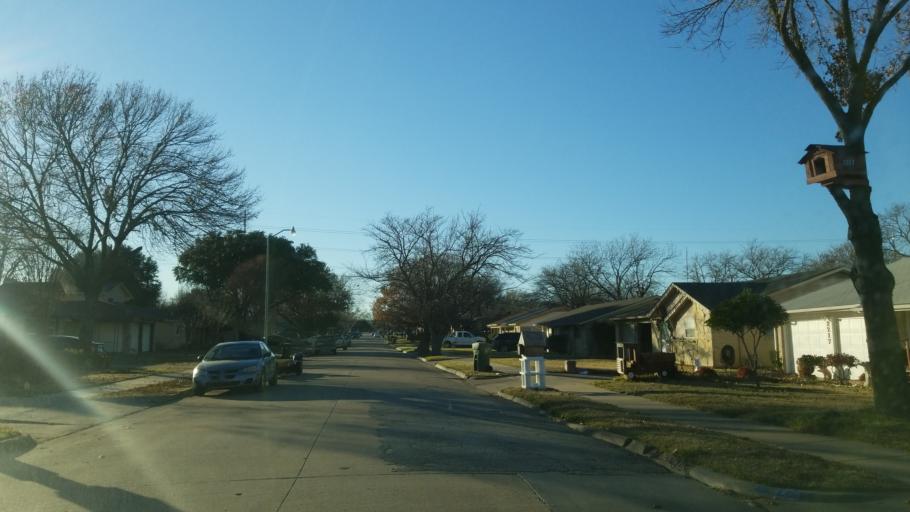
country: US
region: Texas
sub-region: Tarrant County
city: Arlington
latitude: 32.7225
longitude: -97.0696
